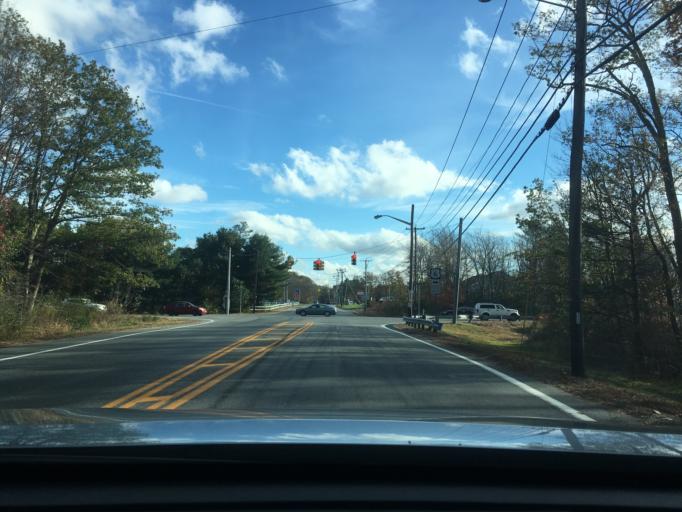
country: US
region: Rhode Island
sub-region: Providence County
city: North Scituate
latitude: 41.8276
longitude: -71.6714
